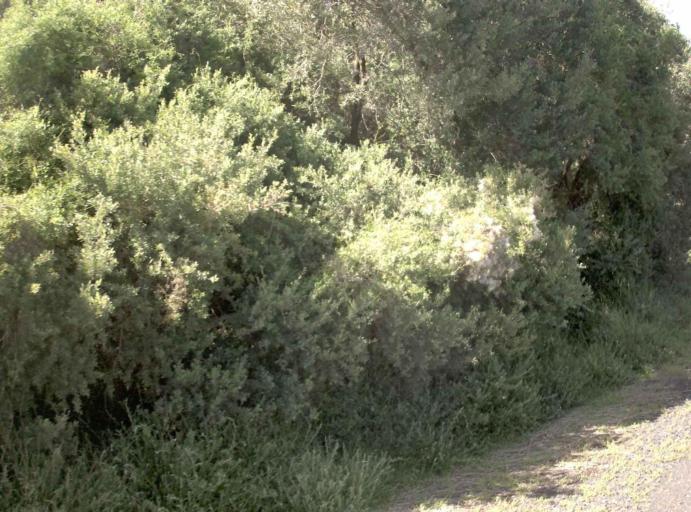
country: AU
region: Victoria
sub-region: Bass Coast
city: Phillip Island
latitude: -38.5030
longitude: 145.1510
